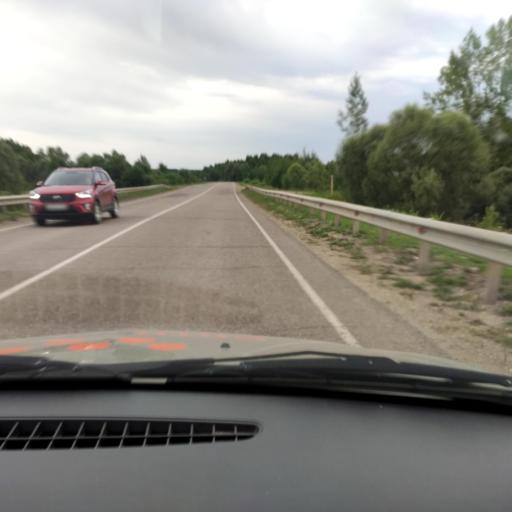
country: RU
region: Bashkortostan
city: Krasnaya Gorka
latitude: 55.1625
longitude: 56.6728
